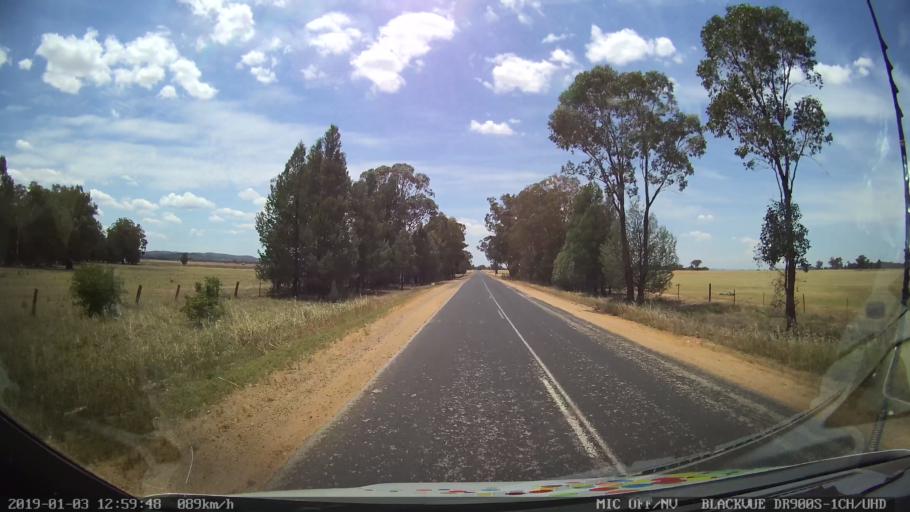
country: AU
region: New South Wales
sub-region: Cabonne
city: Canowindra
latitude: -33.6343
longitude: 148.3942
